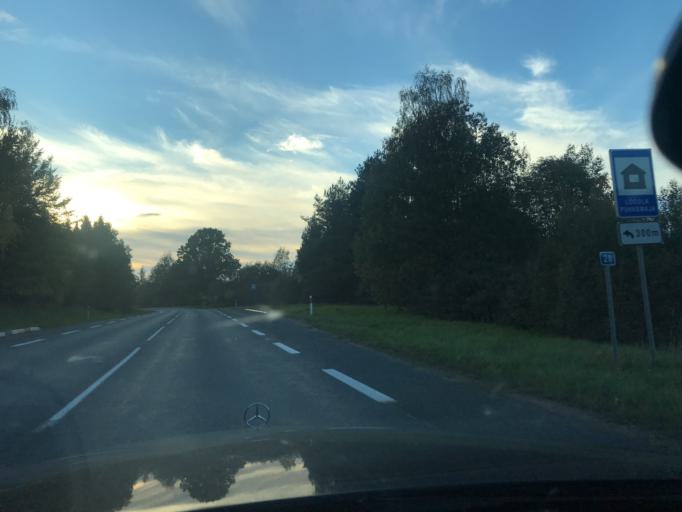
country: EE
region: Vorumaa
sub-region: Antsla vald
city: Vana-Antsla
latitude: 57.8770
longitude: 26.6354
